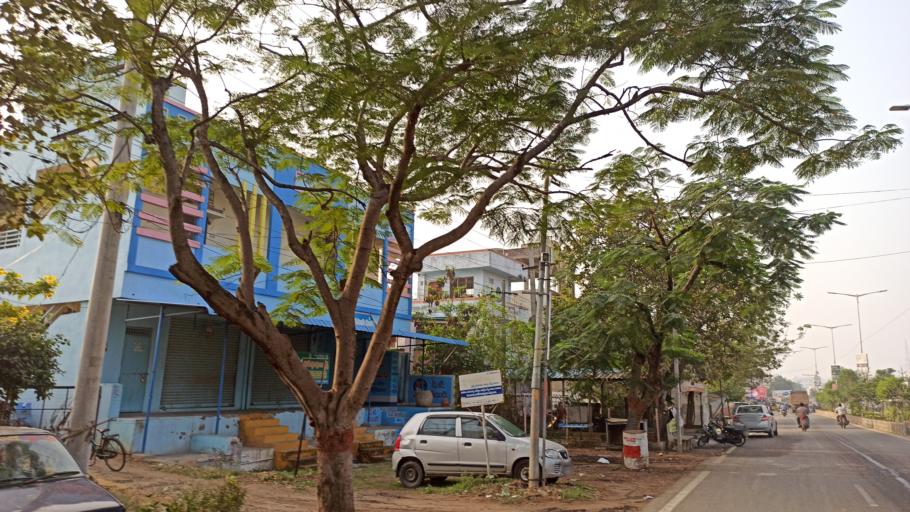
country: IN
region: Andhra Pradesh
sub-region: Guntur
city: Narasaraopet
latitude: 16.2488
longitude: 80.0569
